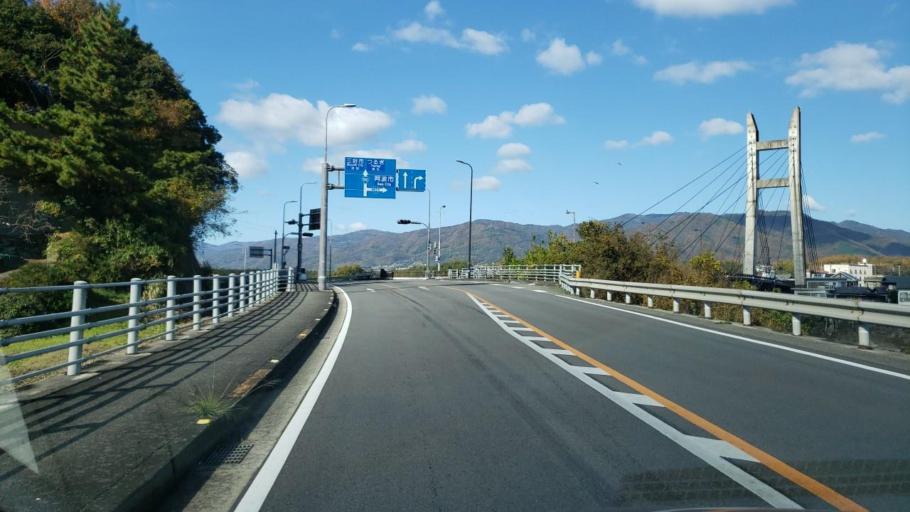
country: JP
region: Tokushima
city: Wakimachi
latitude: 34.0638
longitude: 134.1956
